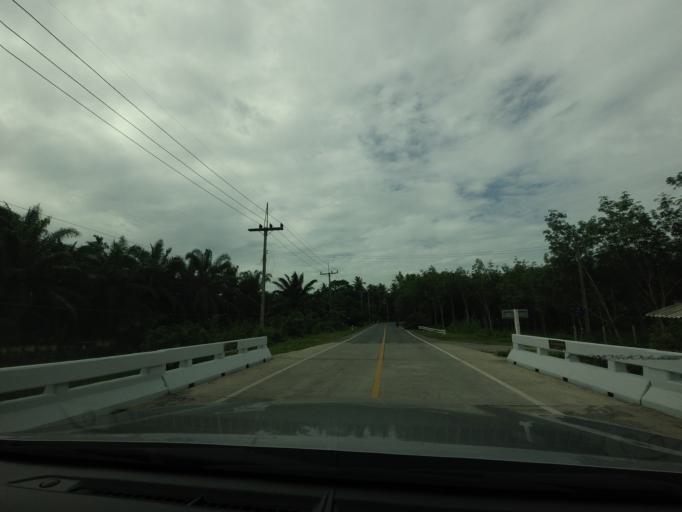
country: TH
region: Nakhon Si Thammarat
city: Phra Phrom
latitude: 8.2922
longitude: 99.9460
